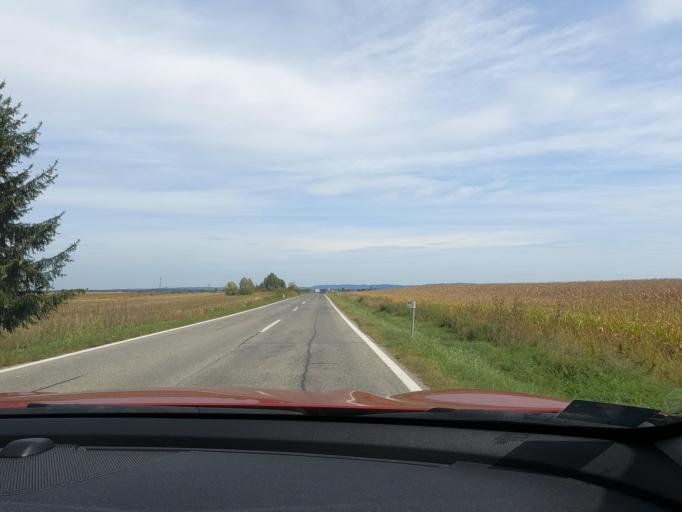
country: HR
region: Sisacko-Moslavacka
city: Osekovo
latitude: 45.5409
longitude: 16.5736
